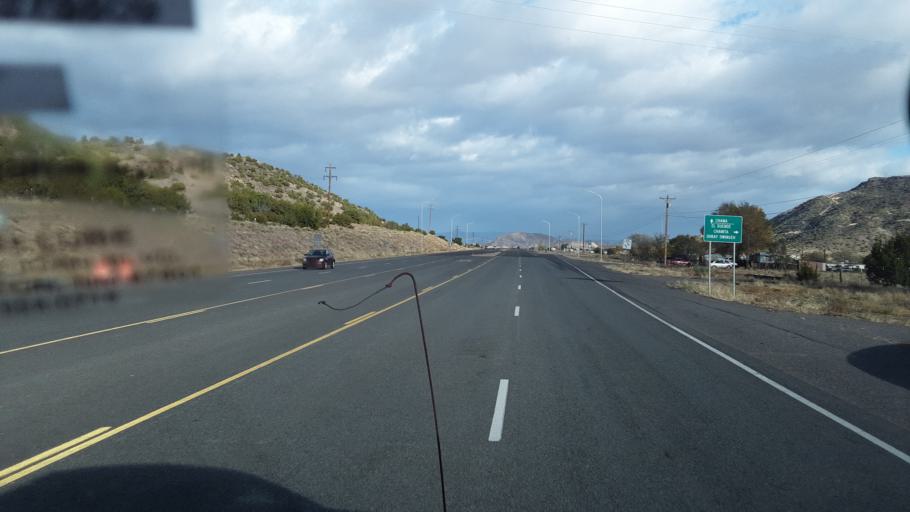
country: US
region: New Mexico
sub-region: Rio Arriba County
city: Ohkay Owingeh
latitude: 36.0703
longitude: -106.1237
